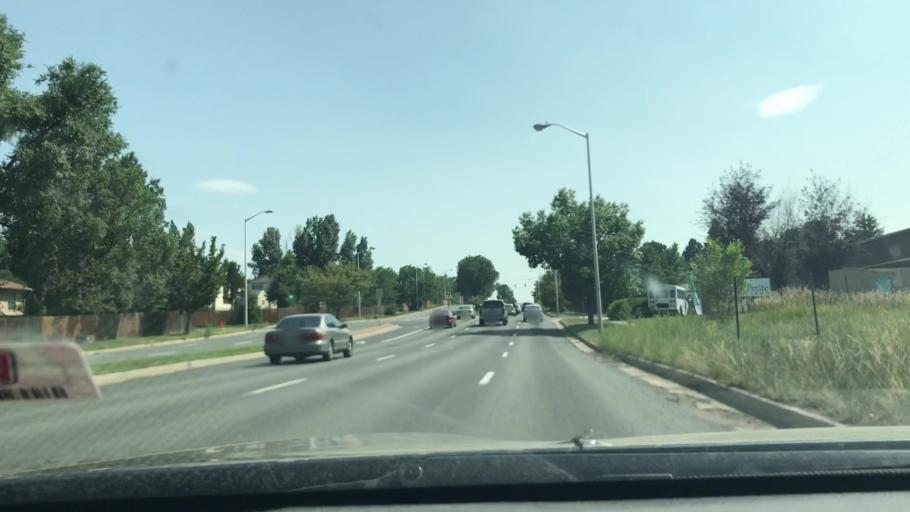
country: US
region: Colorado
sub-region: El Paso County
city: Cimarron Hills
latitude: 38.9242
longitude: -104.7754
